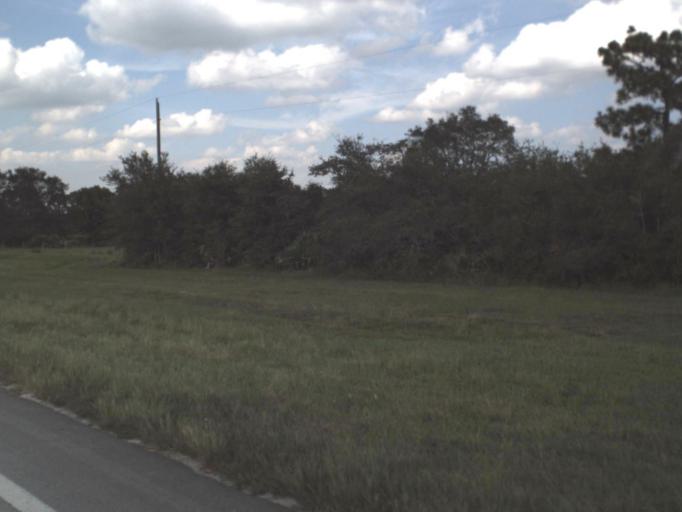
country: US
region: Florida
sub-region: Indian River County
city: Fellsmere
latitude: 27.6298
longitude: -80.8669
